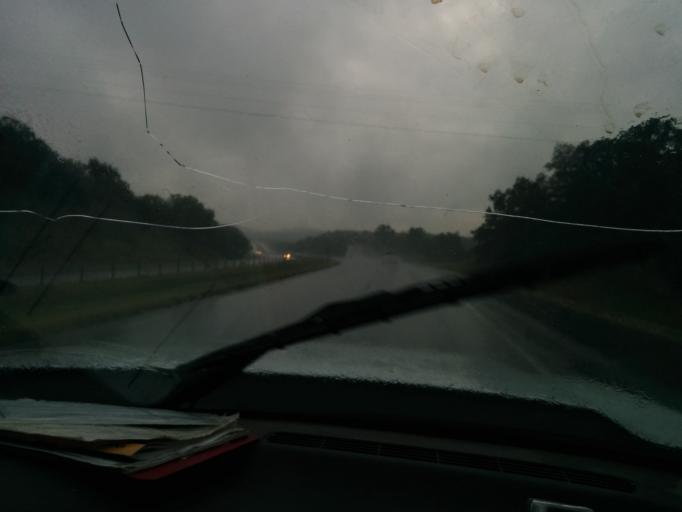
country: US
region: Oklahoma
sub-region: Okmulgee County
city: Beggs
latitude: 35.7309
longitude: -96.0043
